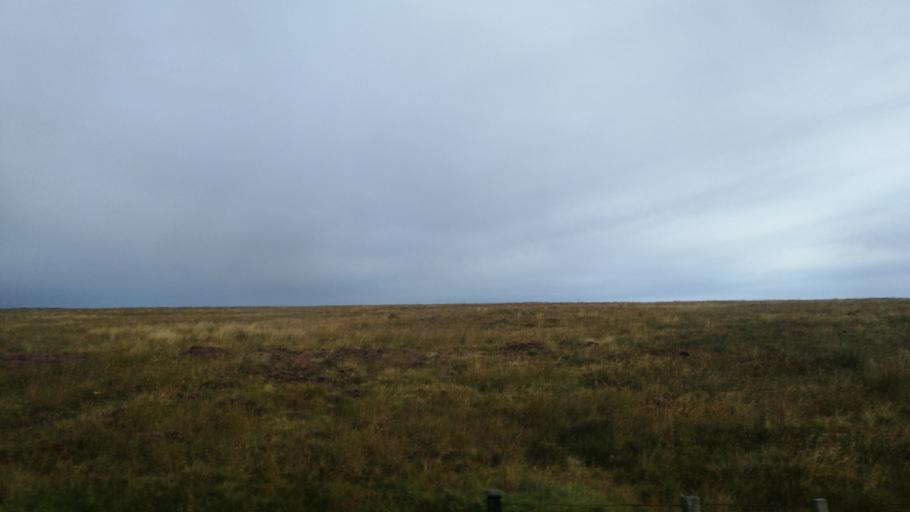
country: GB
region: Scotland
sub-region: Highland
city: Thurso
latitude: 58.4941
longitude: -3.5264
